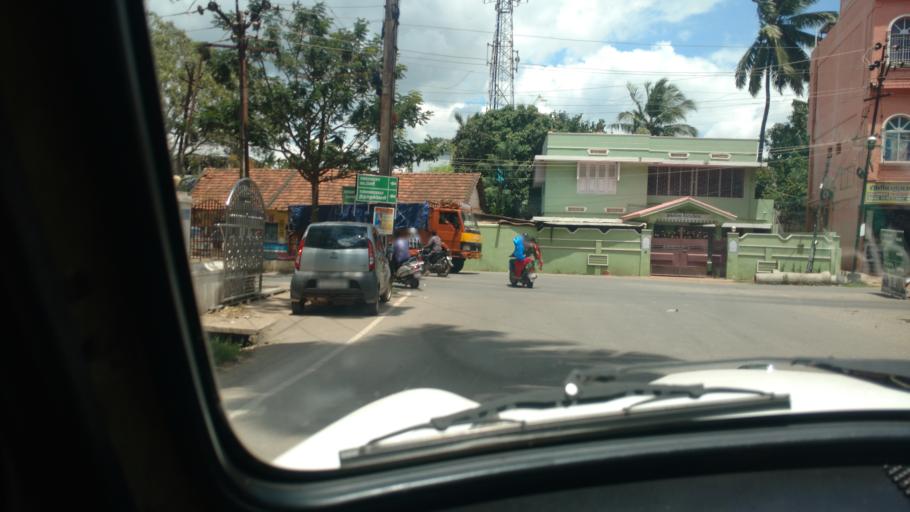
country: IN
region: Tamil Nadu
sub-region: Kanniyakumari
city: Nagercoil
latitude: 8.1892
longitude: 77.4180
